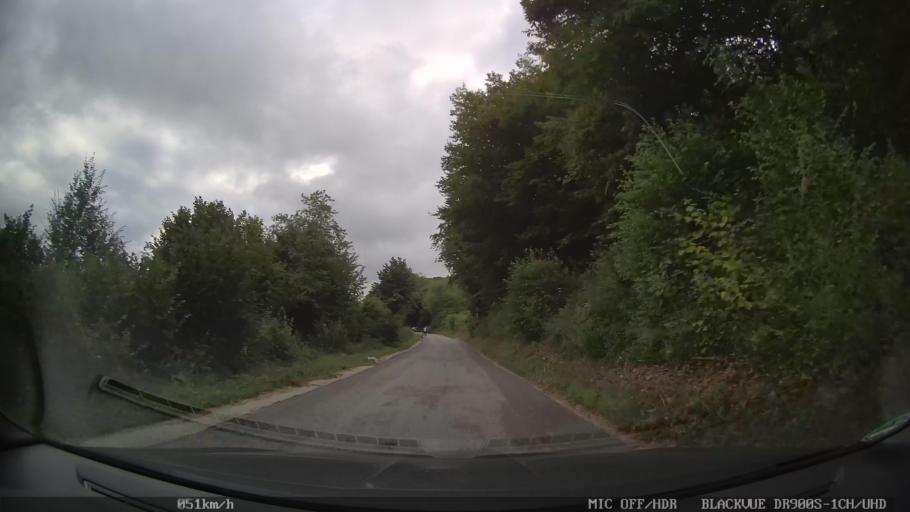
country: HR
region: Licko-Senjska
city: Jezerce
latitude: 44.9271
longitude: 15.6141
